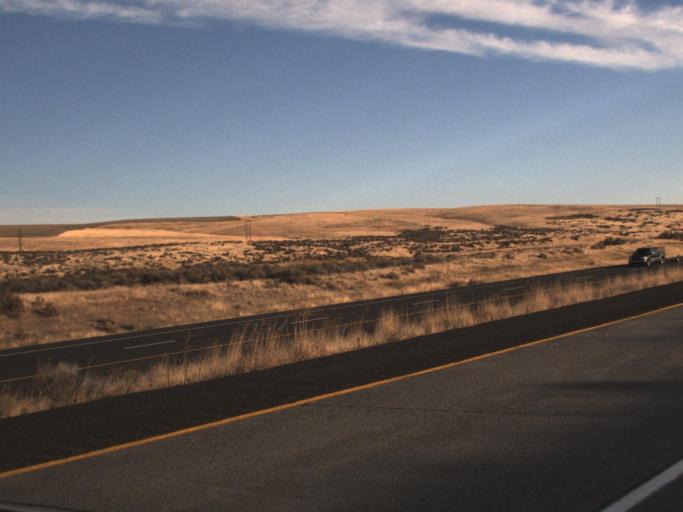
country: US
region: Washington
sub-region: Adams County
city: Ritzville
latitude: 46.9955
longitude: -118.5467
